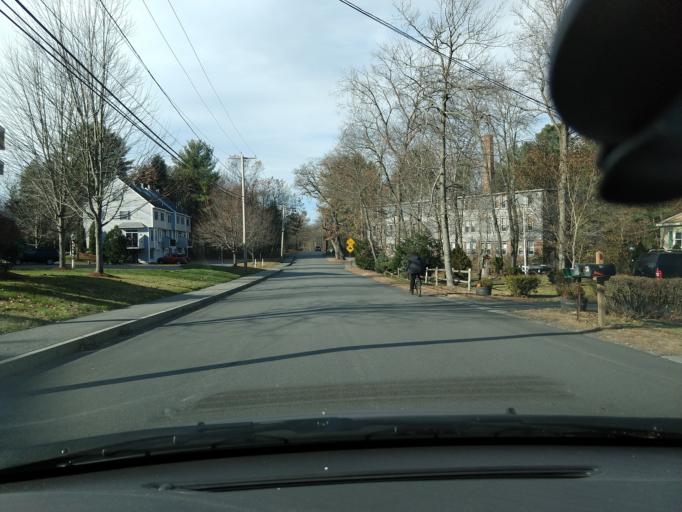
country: US
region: Massachusetts
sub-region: Middlesex County
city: East Pepperell
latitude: 42.6680
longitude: -71.5675
